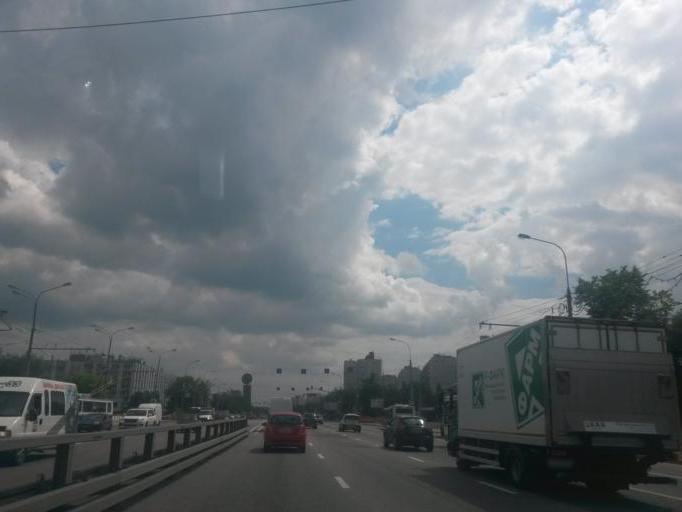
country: RU
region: Moscow
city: Orekhovo-Borisovo
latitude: 55.6029
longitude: 37.7215
